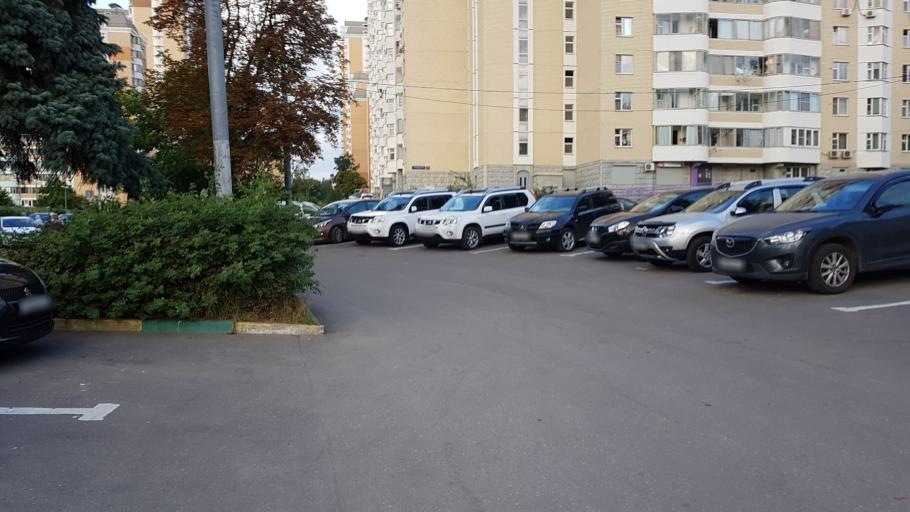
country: RU
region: Moscow
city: Solntsevo
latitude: 55.6539
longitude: 37.4041
